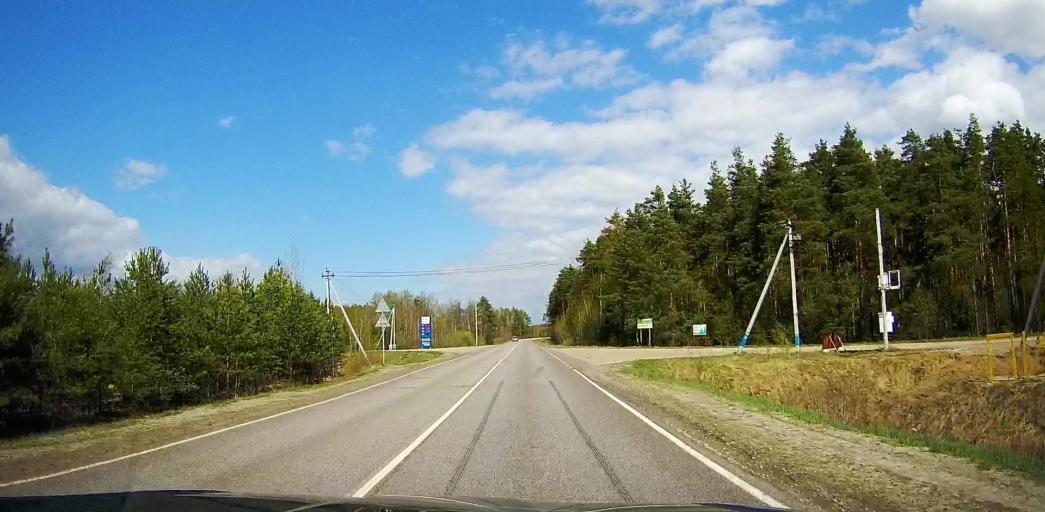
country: RU
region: Moskovskaya
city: Davydovo
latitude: 55.5494
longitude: 38.8173
